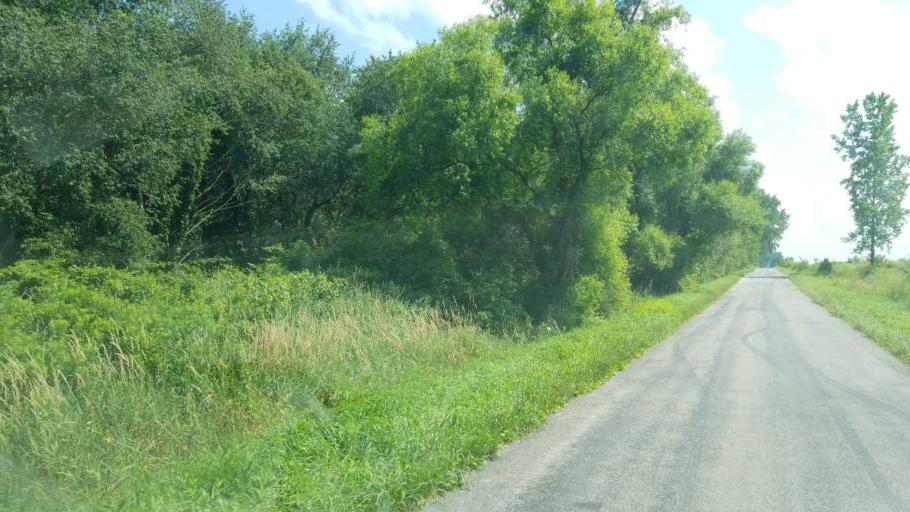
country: US
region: Ohio
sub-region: Huron County
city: Willard
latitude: 41.0157
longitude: -82.7810
